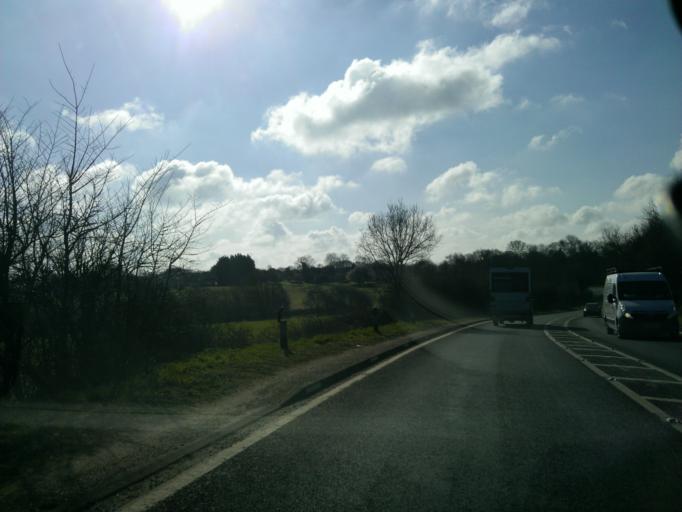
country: GB
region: England
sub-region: Essex
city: Alresford
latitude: 51.8724
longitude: 1.0123
